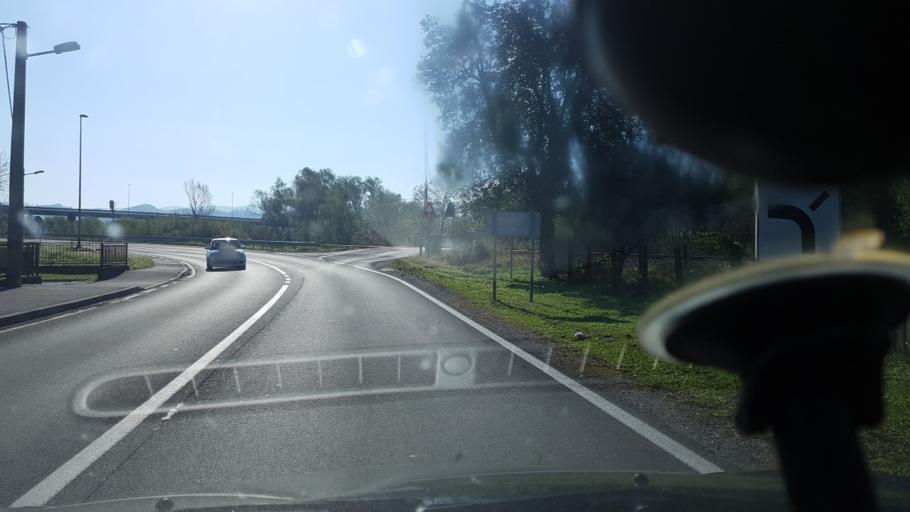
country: HR
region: Krapinsko-Zagorska
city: Zabok
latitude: 46.0188
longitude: 15.9302
